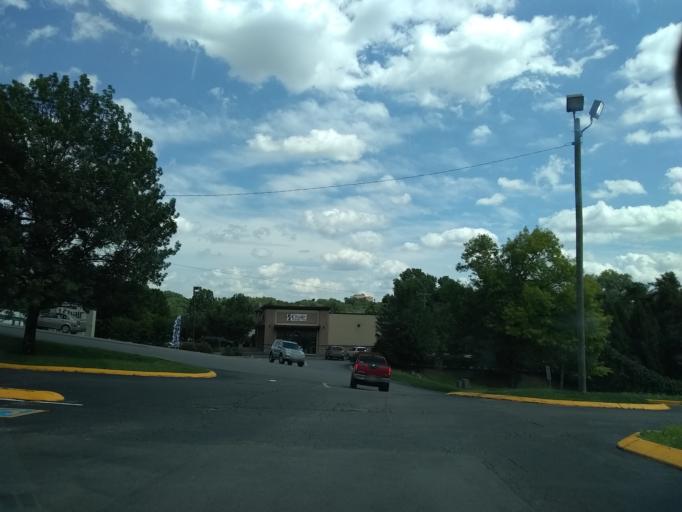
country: US
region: Tennessee
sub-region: Davidson County
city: Nashville
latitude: 36.1373
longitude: -86.7005
